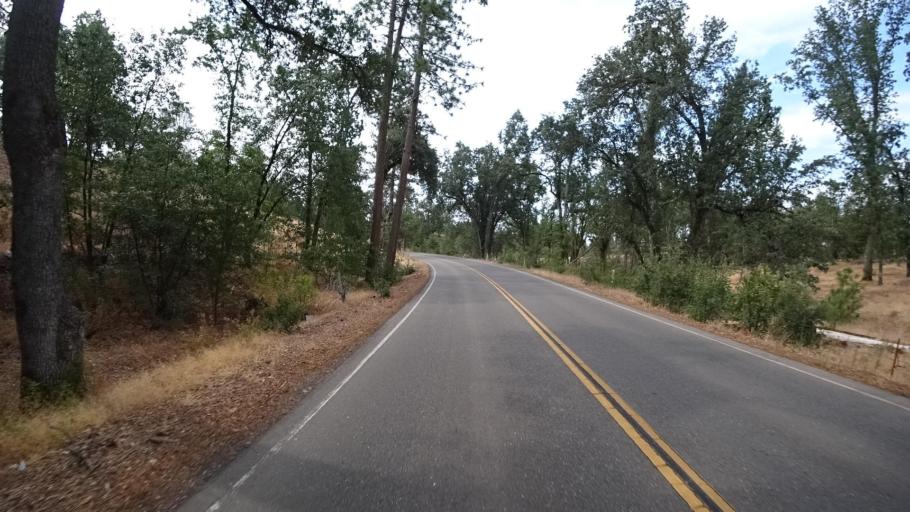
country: US
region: California
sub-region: Mariposa County
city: Midpines
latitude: 37.5292
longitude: -119.9477
